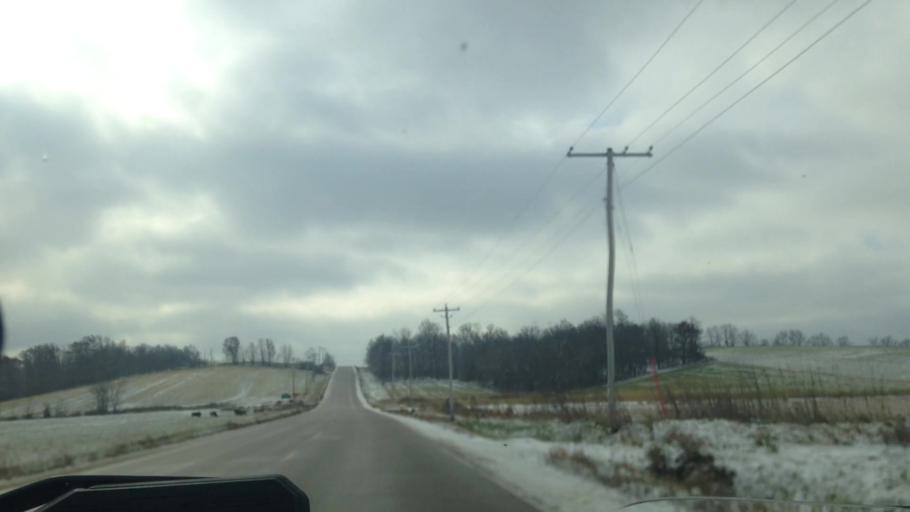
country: US
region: Wisconsin
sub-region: Dodge County
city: Mayville
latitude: 43.4645
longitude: -88.5000
